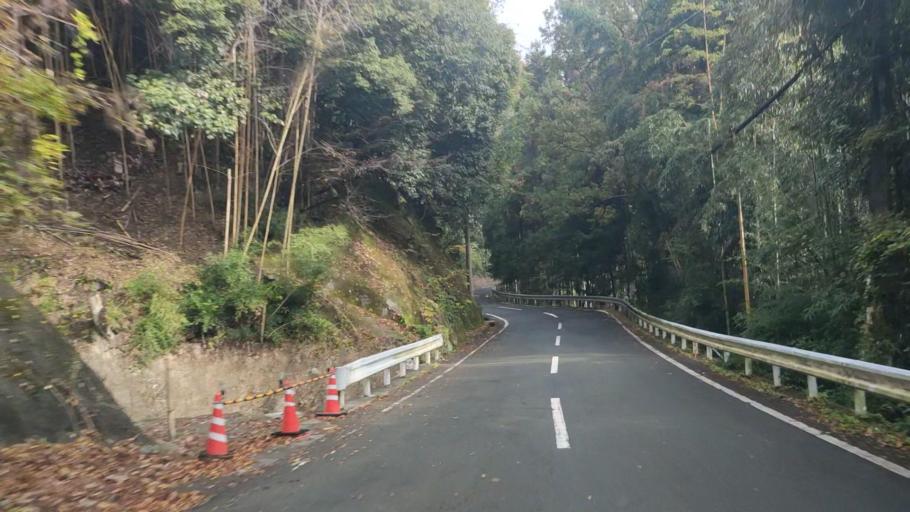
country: JP
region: Shizuoka
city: Fujinomiya
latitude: 35.3582
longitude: 138.4403
